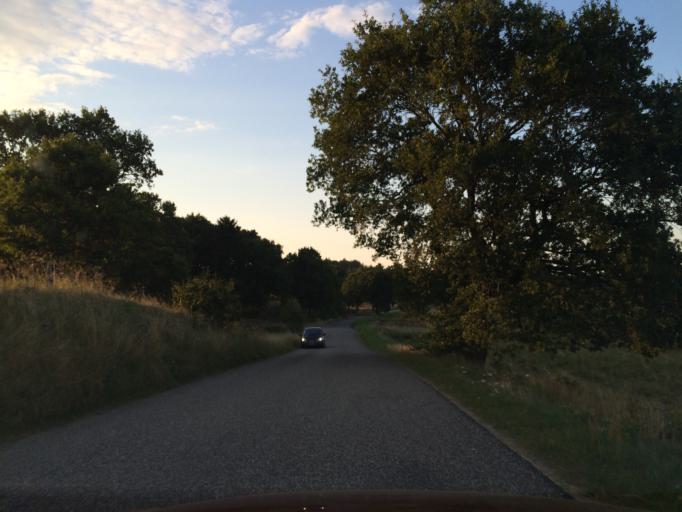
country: DK
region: Central Jutland
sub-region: Silkeborg Kommune
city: Svejbaek
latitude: 56.1992
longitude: 9.6463
